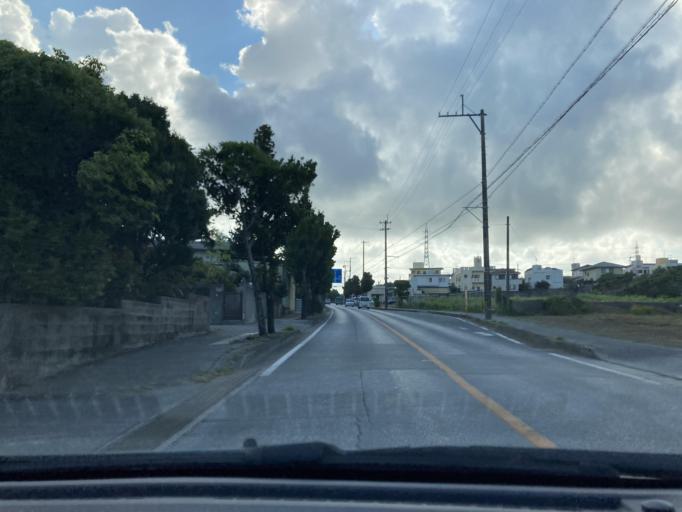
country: JP
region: Okinawa
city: Tomigusuku
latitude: 26.1746
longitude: 127.7225
